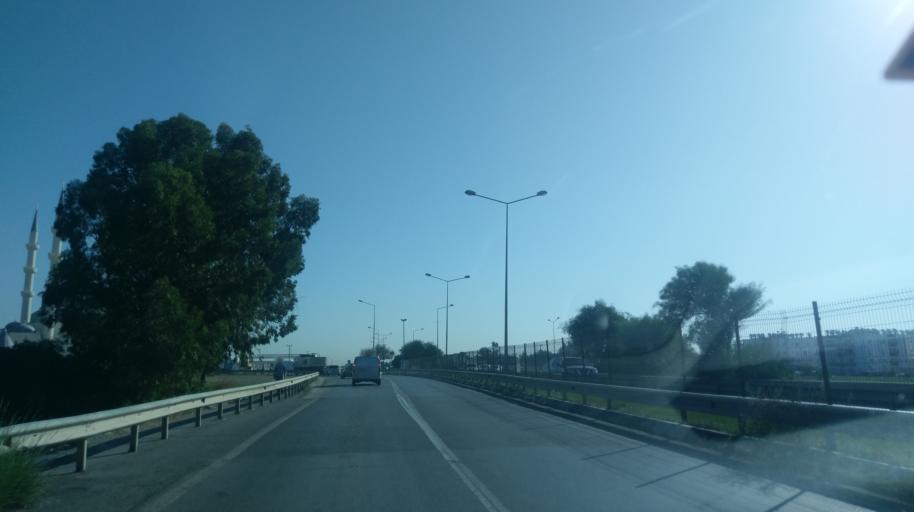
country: CY
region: Lefkosia
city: Nicosia
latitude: 35.2172
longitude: 33.4206
